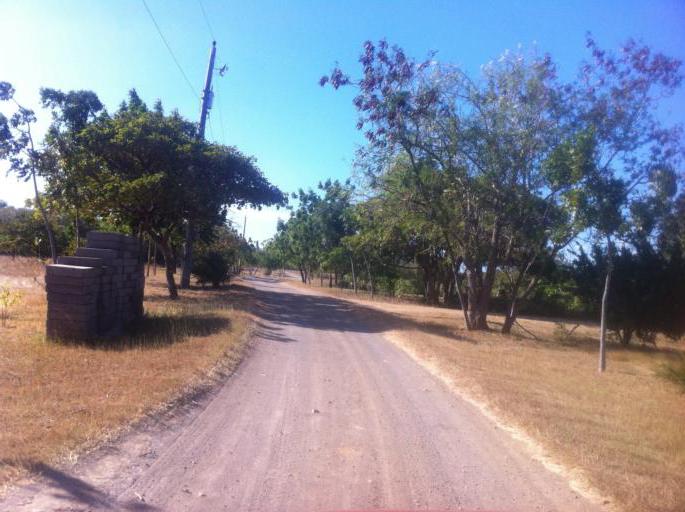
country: NI
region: Managua
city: Carlos Fonseca Amador
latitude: 11.9003
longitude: -86.6074
